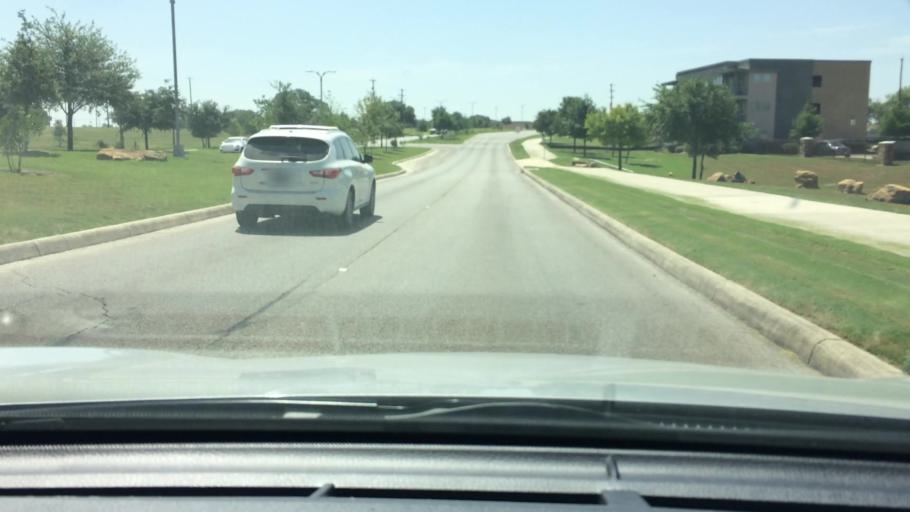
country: US
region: Texas
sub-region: Bexar County
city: San Antonio
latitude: 29.3479
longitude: -98.4473
